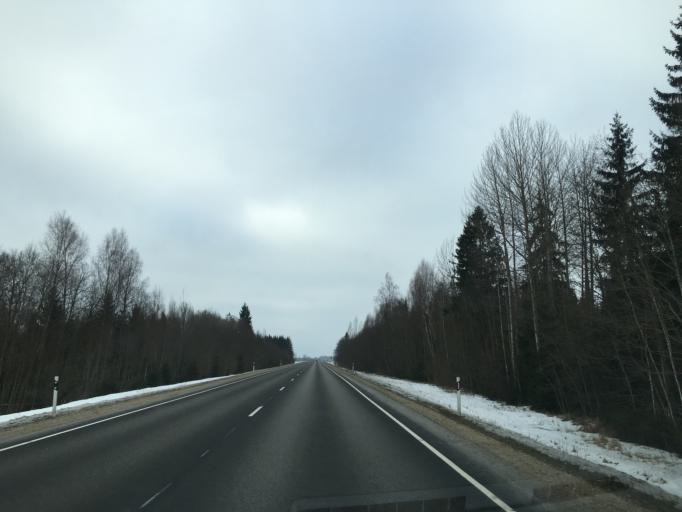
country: EE
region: Tartu
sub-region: Elva linn
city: Elva
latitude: 58.2077
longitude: 26.3595
